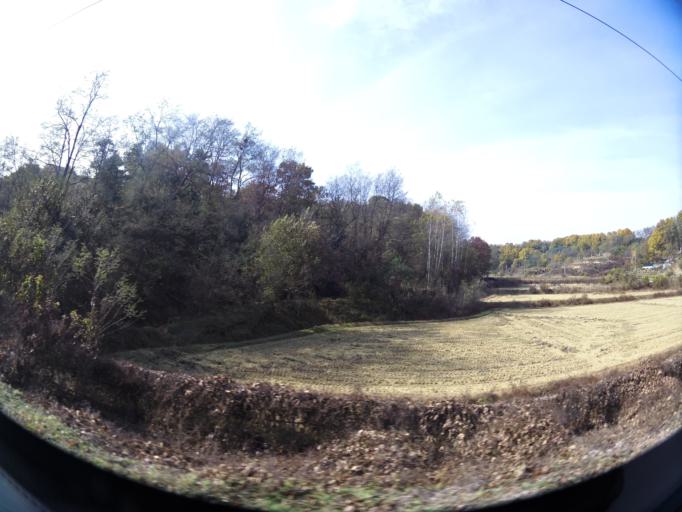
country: KR
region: Daejeon
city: Sintansin
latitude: 36.4758
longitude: 127.4223
